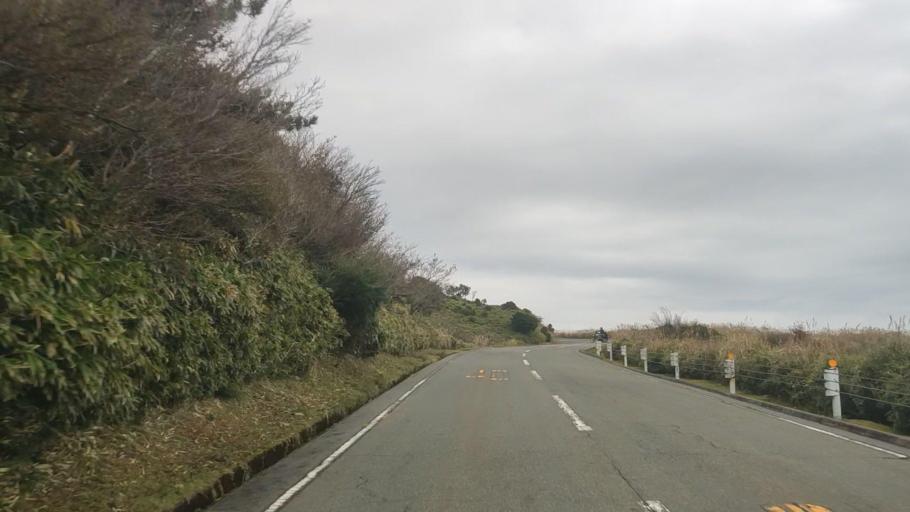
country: JP
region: Shizuoka
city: Heda
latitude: 34.9519
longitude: 138.8403
